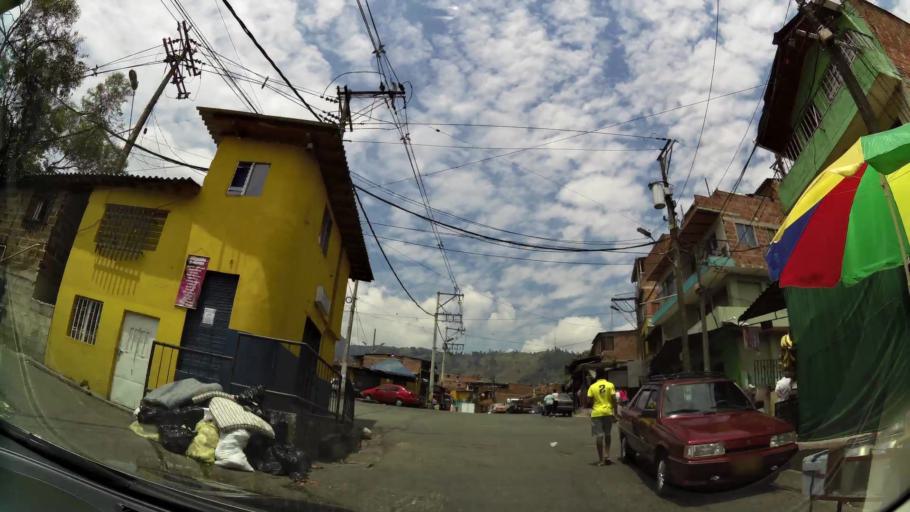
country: CO
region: Antioquia
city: Bello
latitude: 6.3098
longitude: -75.5780
